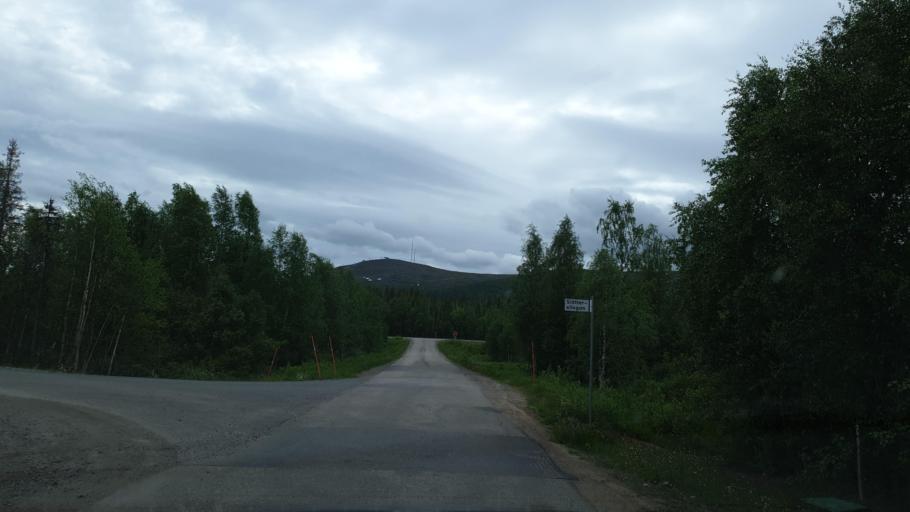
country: SE
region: Norrbotten
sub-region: Gallivare Kommun
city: Gaellivare
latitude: 67.1306
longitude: 20.6262
